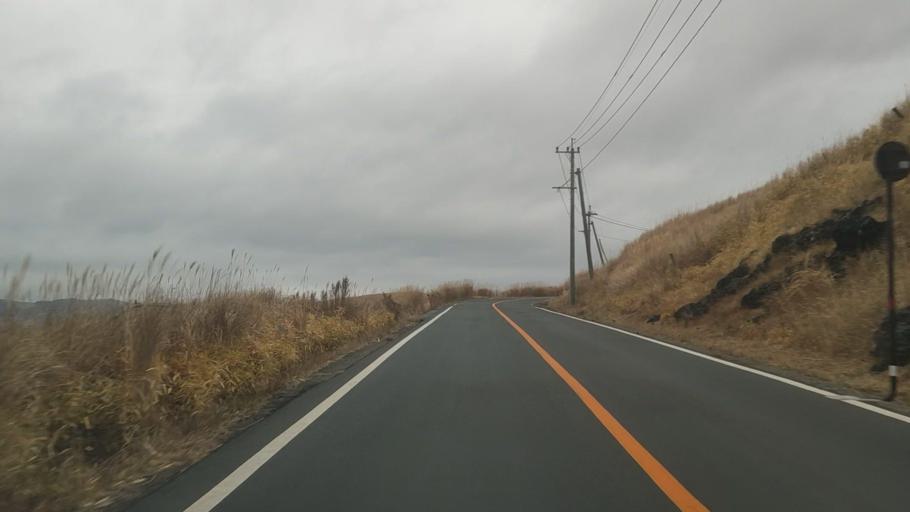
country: JP
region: Kumamoto
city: Aso
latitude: 32.9018
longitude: 131.0297
